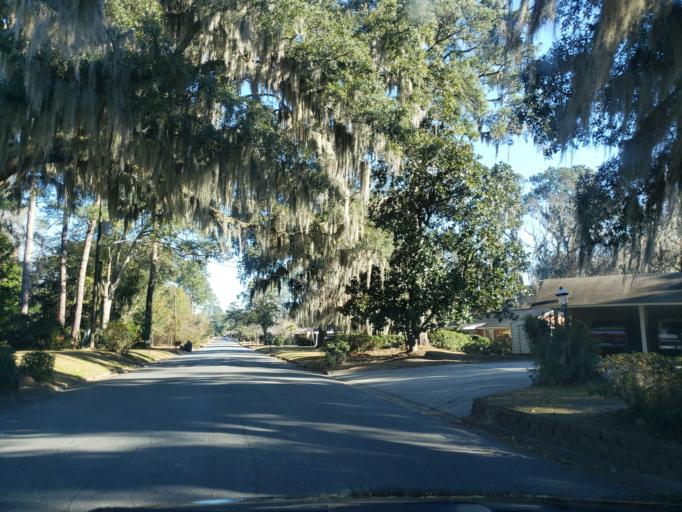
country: US
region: Georgia
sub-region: Chatham County
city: Thunderbolt
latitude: 32.0193
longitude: -81.1000
